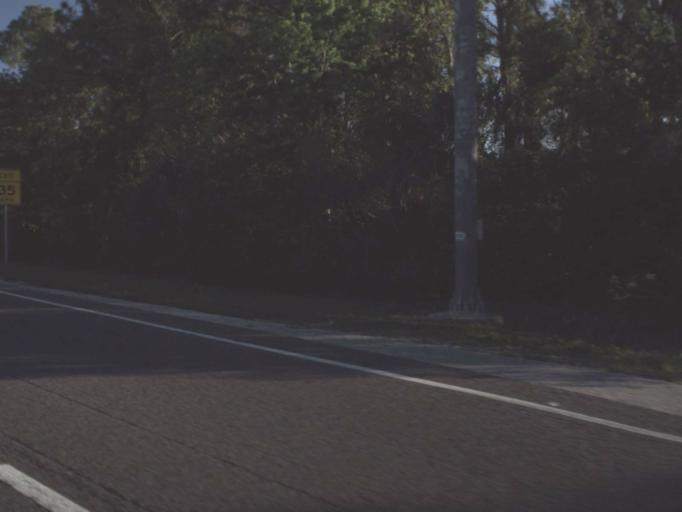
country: US
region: Florida
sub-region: Flagler County
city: Flagler Beach
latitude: 29.4072
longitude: -81.1569
